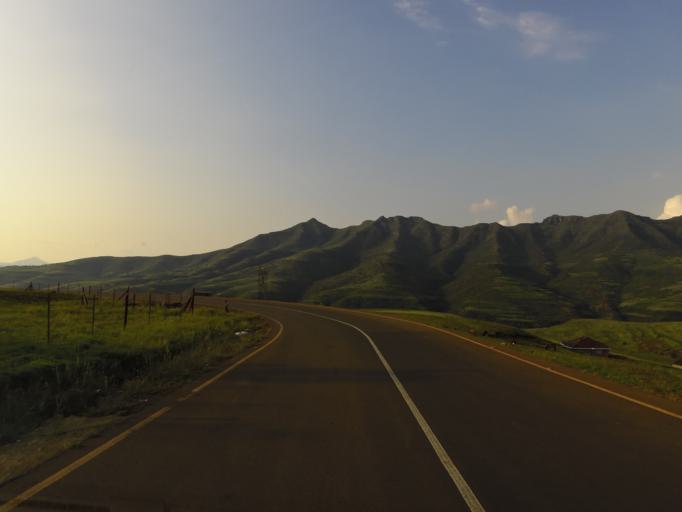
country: LS
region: Butha-Buthe
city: Butha-Buthe
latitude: -29.0337
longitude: 28.2863
